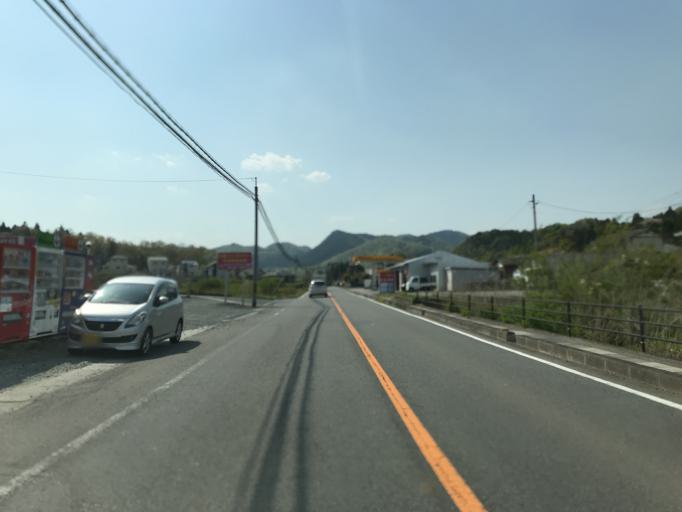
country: JP
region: Fukushima
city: Iwaki
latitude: 36.9521
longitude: 140.7644
